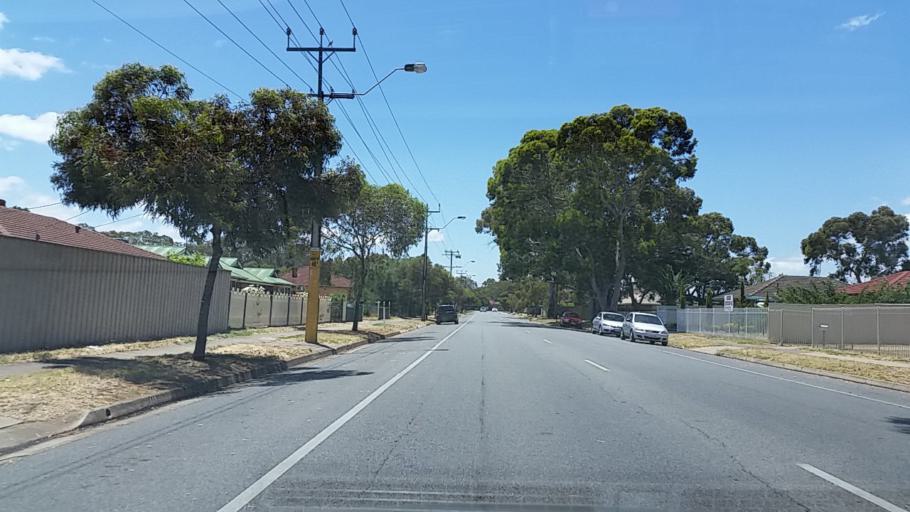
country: AU
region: South Australia
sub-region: Salisbury
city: Salisbury
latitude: -34.7647
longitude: 138.6277
